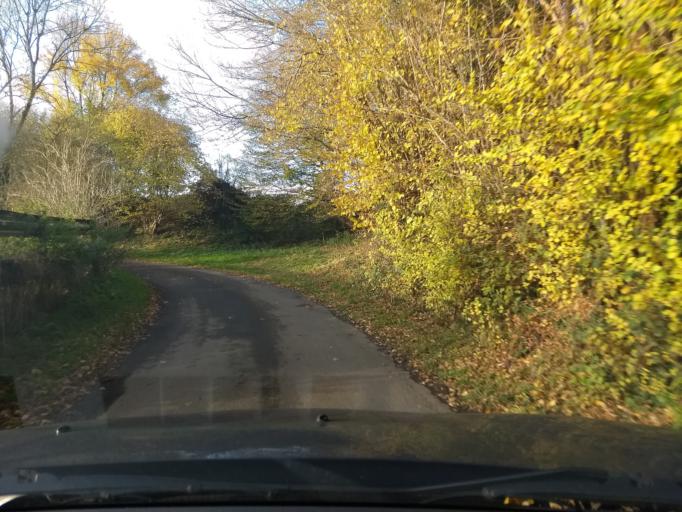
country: BE
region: Wallonia
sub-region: Province du Brabant Wallon
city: Nivelles
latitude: 50.6006
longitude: 4.2880
